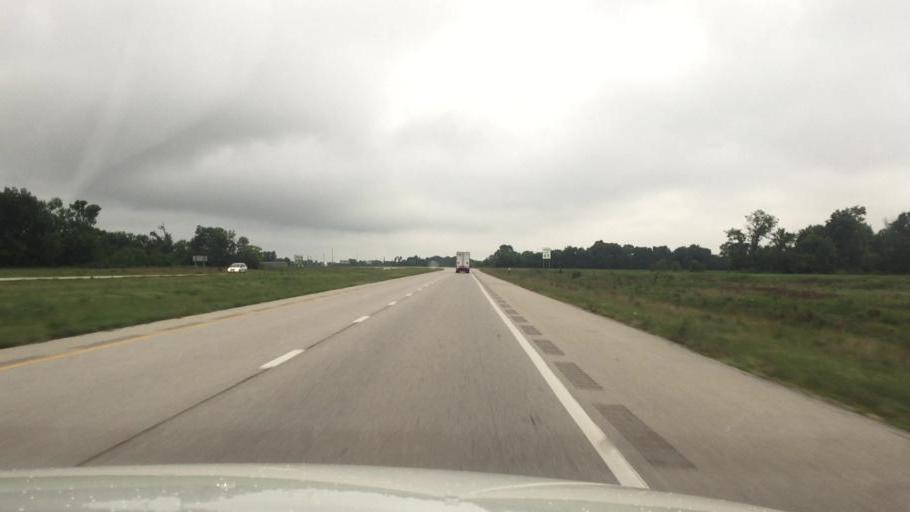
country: US
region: Kansas
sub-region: Montgomery County
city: Coffeyville
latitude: 37.1062
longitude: -95.5876
